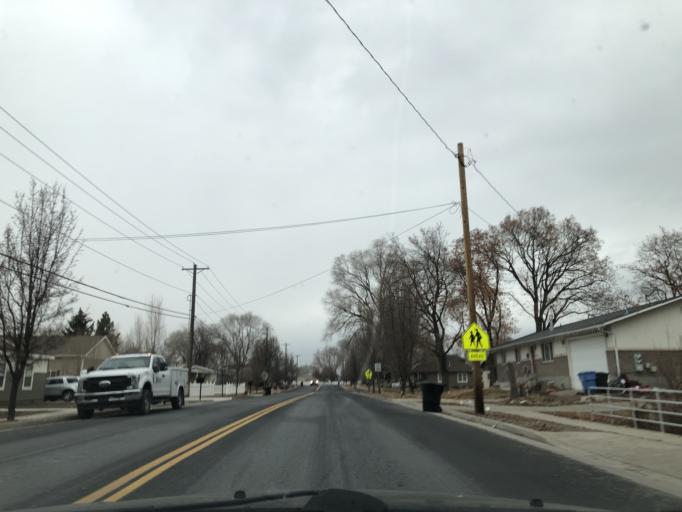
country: US
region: Utah
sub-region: Cache County
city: Logan
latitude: 41.7214
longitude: -111.8532
